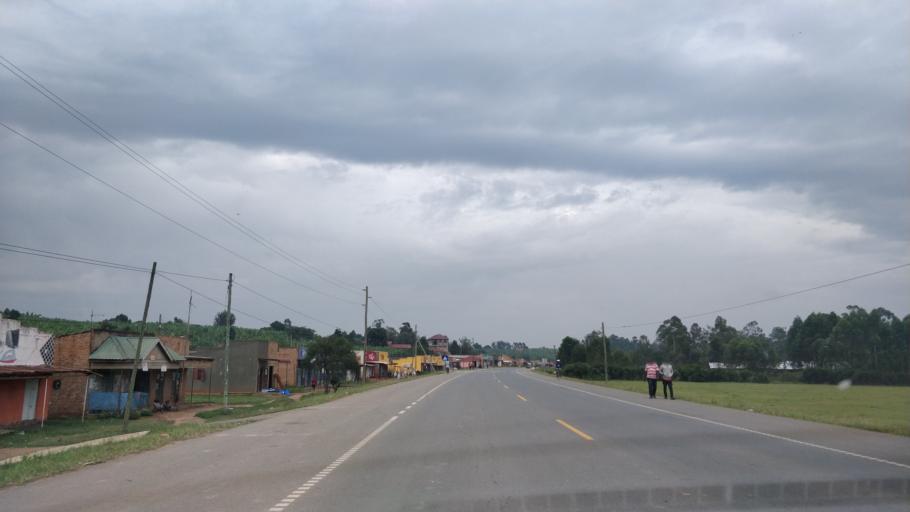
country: UG
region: Western Region
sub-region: Sheema District
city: Kibingo
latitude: -0.6613
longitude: 30.4547
